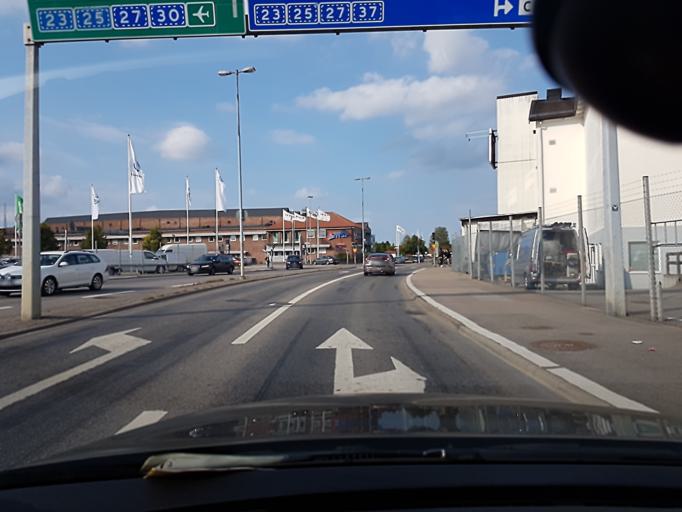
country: SE
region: Kronoberg
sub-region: Vaxjo Kommun
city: Vaexjoe
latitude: 56.8782
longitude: 14.7854
